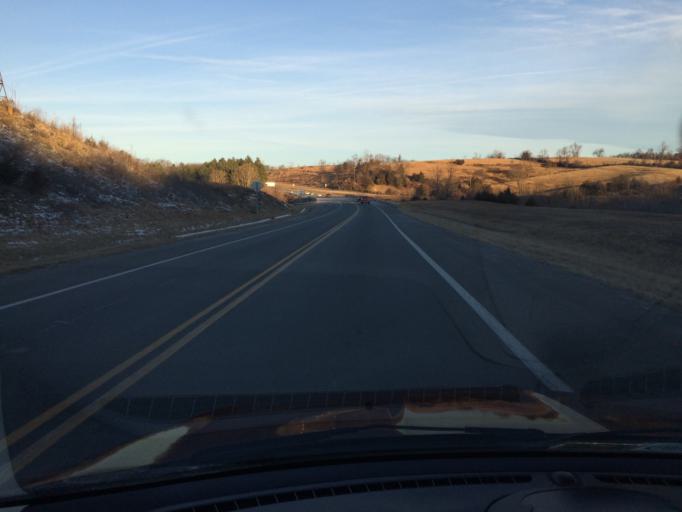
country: US
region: Virginia
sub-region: Augusta County
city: Jolivue
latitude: 38.1303
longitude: -79.0917
